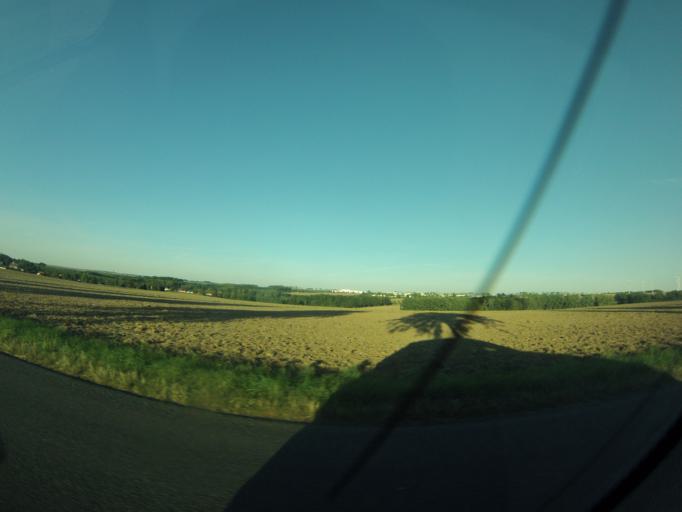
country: DE
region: Thuringia
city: Schmolln
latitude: 50.8861
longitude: 12.3661
